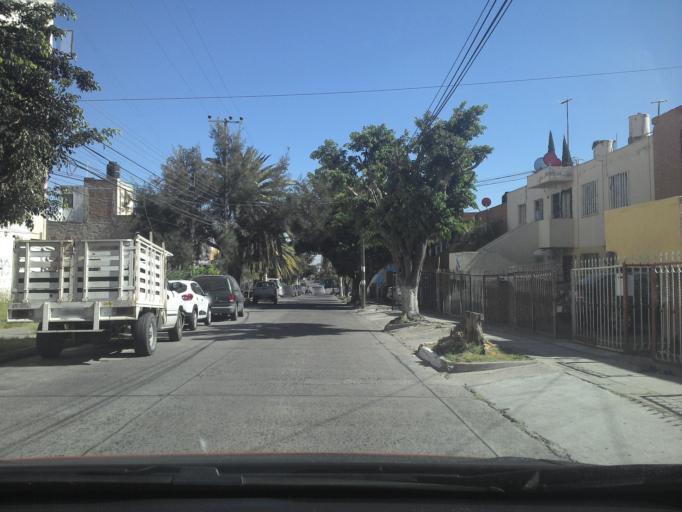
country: MX
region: Jalisco
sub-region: Zapopan
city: Zapopan
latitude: 20.7436
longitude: -103.4006
